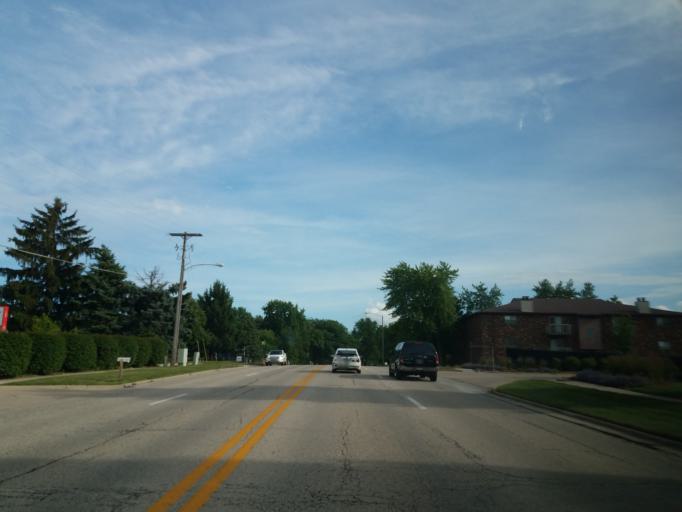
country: US
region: Illinois
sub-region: McLean County
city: Normal
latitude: 40.5003
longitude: -88.9387
